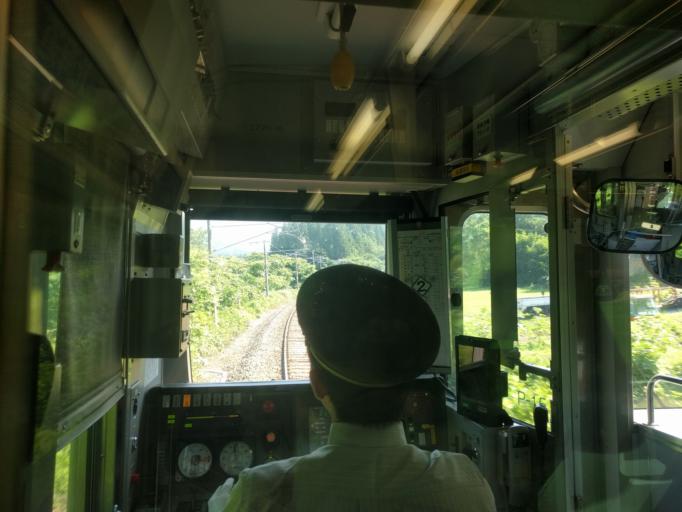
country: JP
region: Fukushima
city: Inawashiro
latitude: 37.5543
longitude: 140.0062
